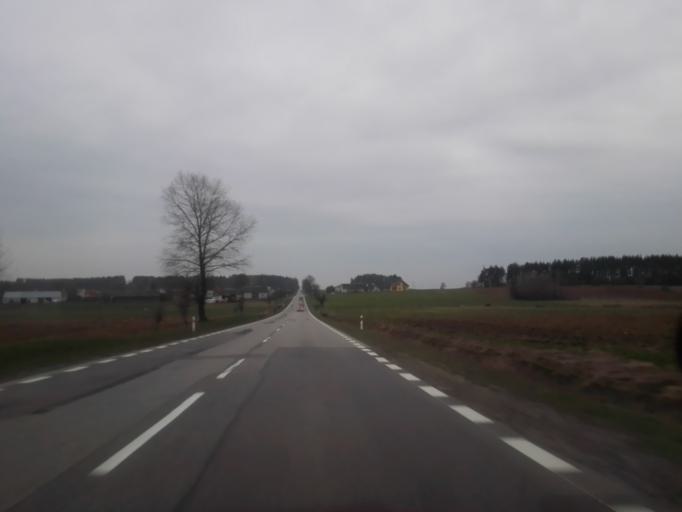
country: PL
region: Podlasie
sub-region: Powiat lomzynski
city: Piatnica
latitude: 53.2785
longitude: 22.1363
